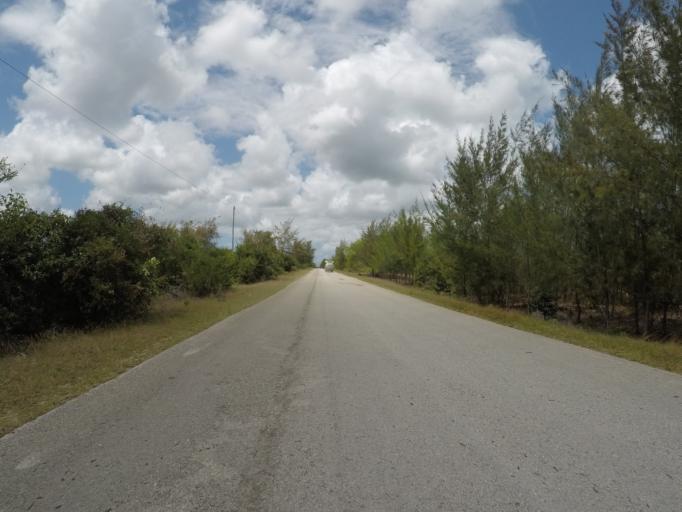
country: TZ
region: Zanzibar Central/South
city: Mahonda
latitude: -6.3236
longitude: 39.4355
